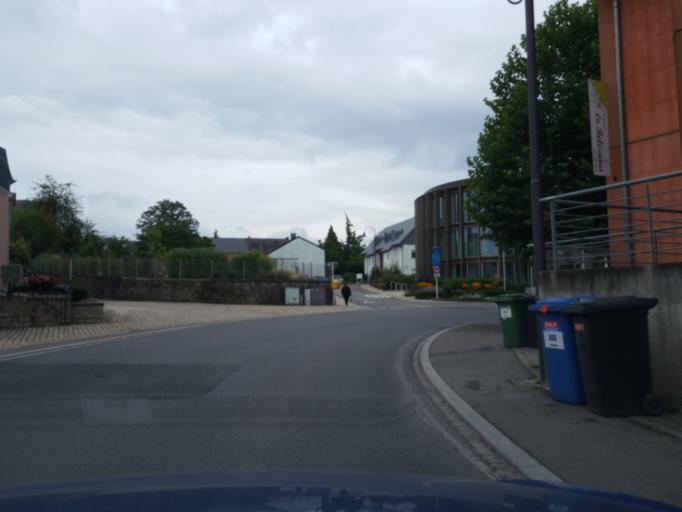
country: LU
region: Luxembourg
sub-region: Canton de Capellen
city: Kehlen
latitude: 49.6682
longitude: 6.0344
